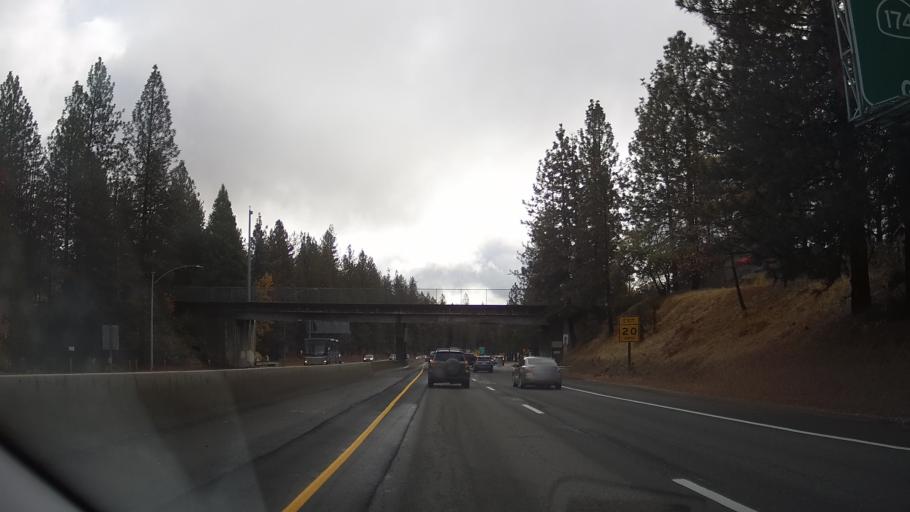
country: US
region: California
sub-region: Placer County
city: Colfax
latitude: 39.0967
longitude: -120.9495
